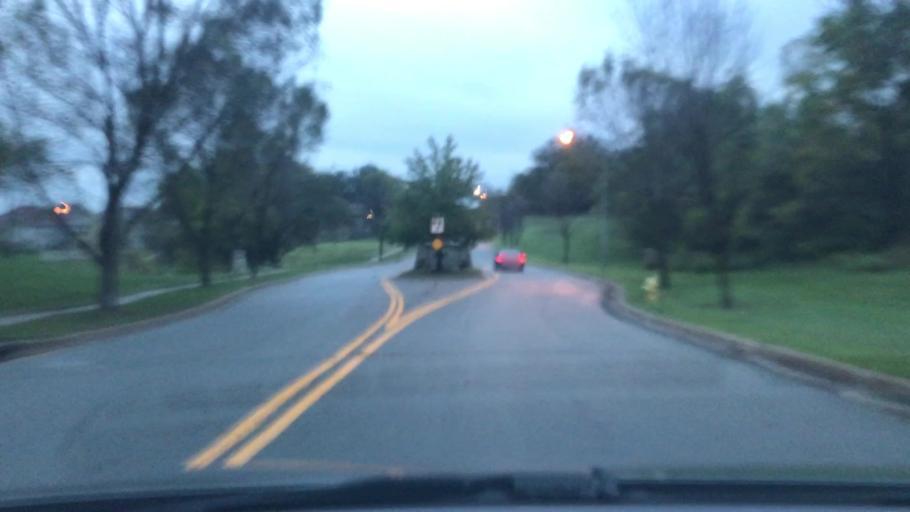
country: US
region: Missouri
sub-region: Jackson County
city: Blue Springs
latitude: 38.9897
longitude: -94.3586
